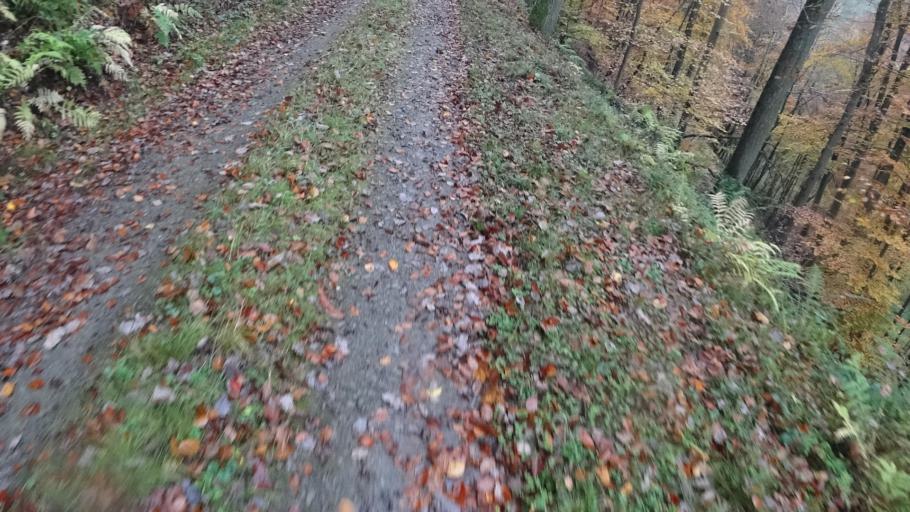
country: DE
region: Rheinland-Pfalz
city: Utzenhain
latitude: 50.1520
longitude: 7.6425
